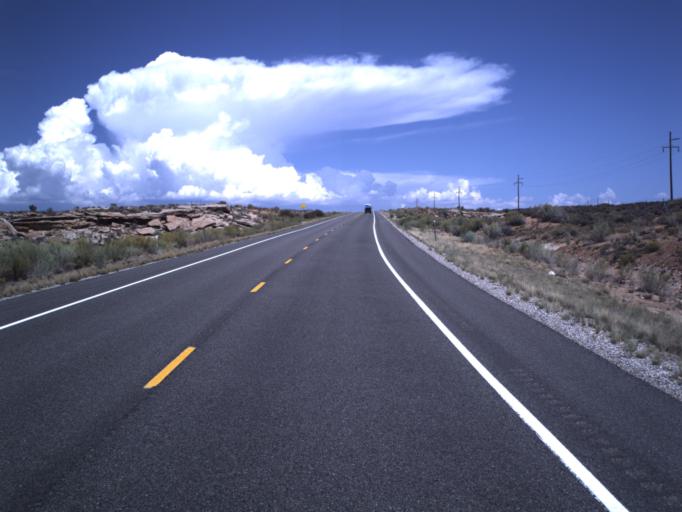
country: US
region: Utah
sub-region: San Juan County
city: Blanding
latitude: 37.3737
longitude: -109.5056
